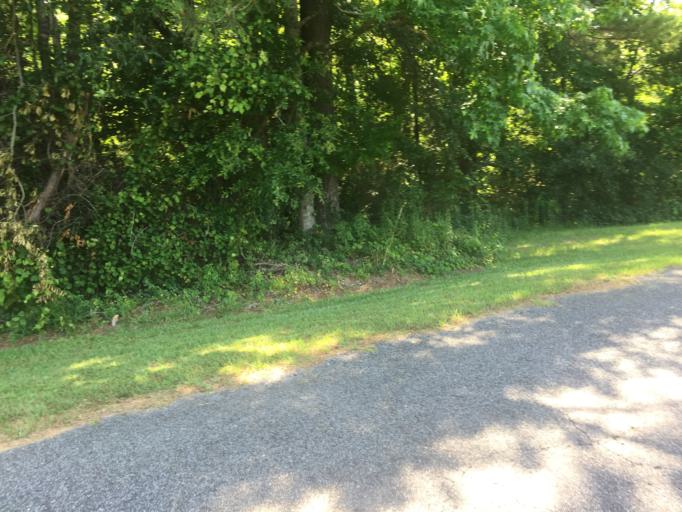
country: US
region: Alabama
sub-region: Hale County
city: Moundville
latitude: 33.0052
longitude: -87.6278
